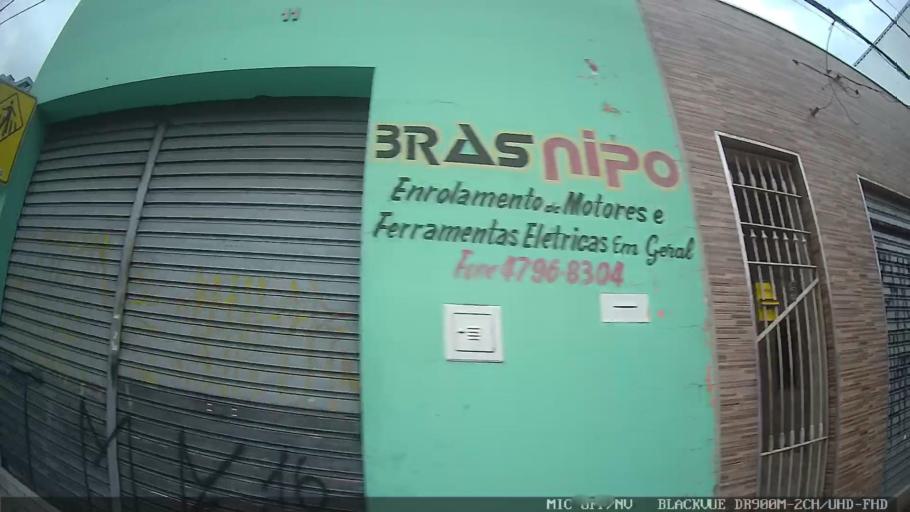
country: BR
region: Sao Paulo
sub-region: Mogi das Cruzes
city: Mogi das Cruzes
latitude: -23.5251
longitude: -46.1919
